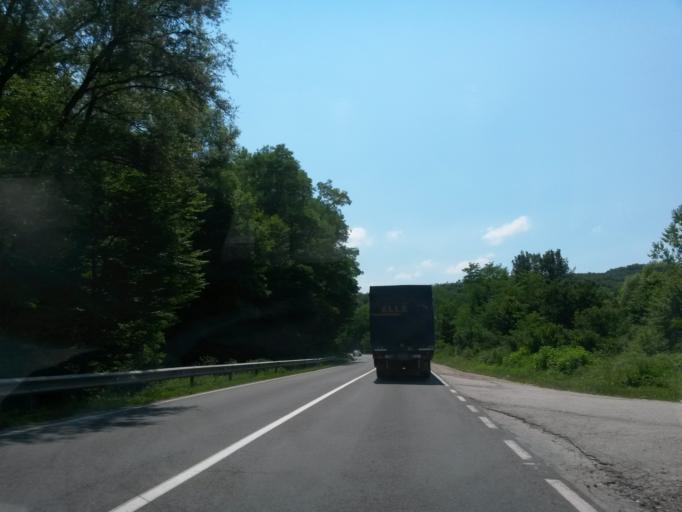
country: BA
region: Federation of Bosnia and Herzegovina
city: Lijesnica
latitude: 44.4650
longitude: 18.0658
